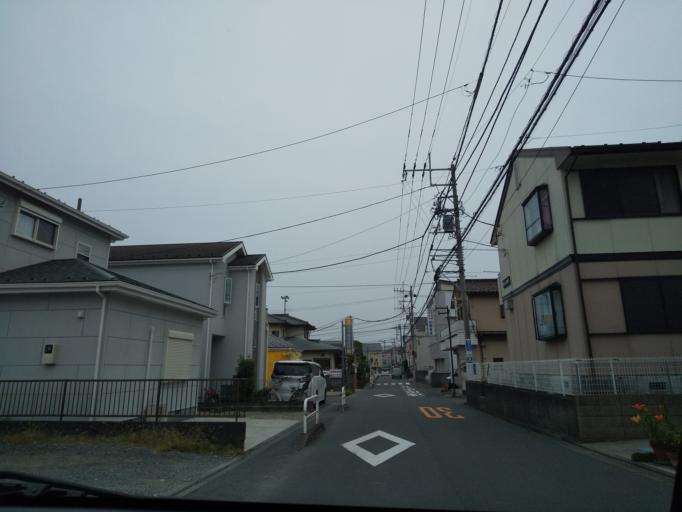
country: JP
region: Kanagawa
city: Zama
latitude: 35.5011
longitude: 139.4049
